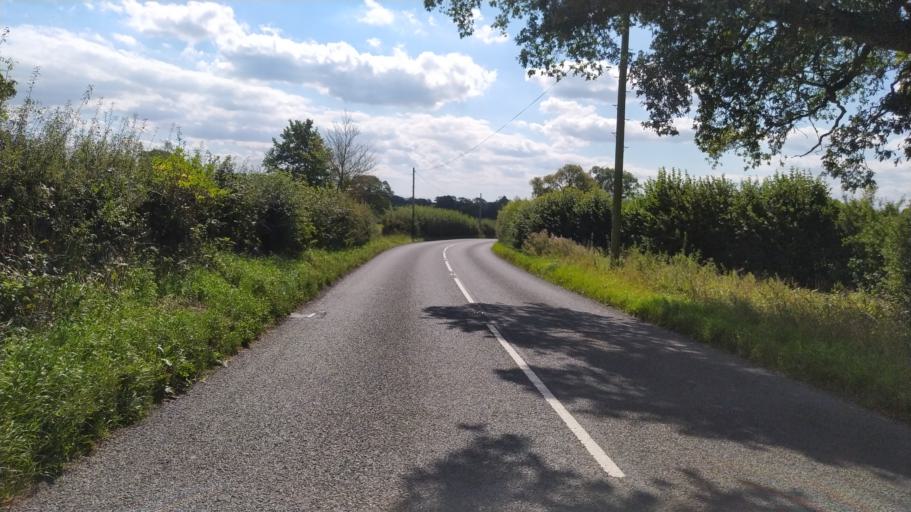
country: GB
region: England
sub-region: Wiltshire
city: Mere
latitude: 51.0862
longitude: -2.2812
